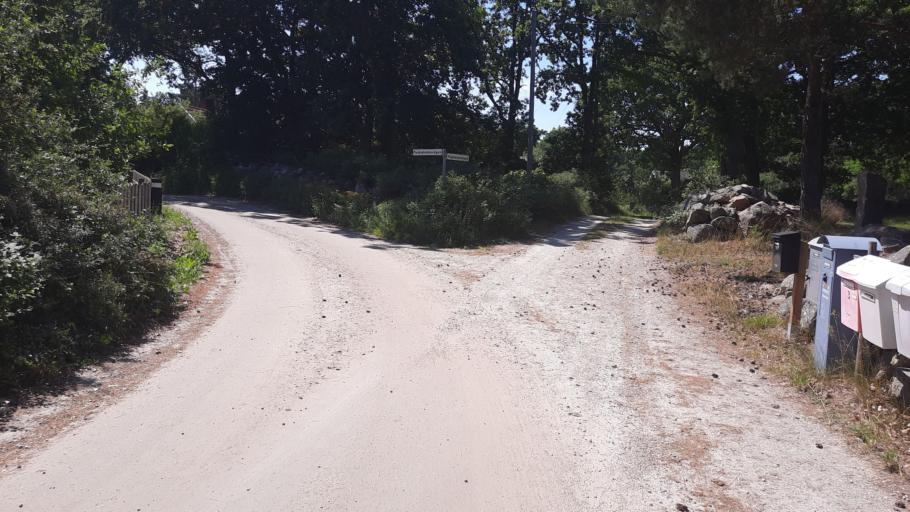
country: SE
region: Blekinge
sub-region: Karlskrona Kommun
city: Jaemjoe
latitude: 56.1516
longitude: 15.7565
